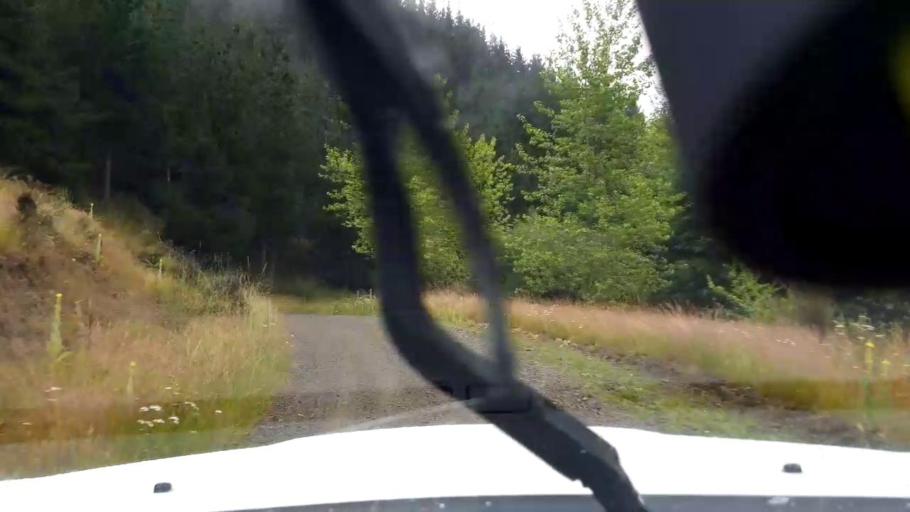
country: NZ
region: Canterbury
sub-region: Timaru District
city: Pleasant Point
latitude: -44.0336
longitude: 171.0040
